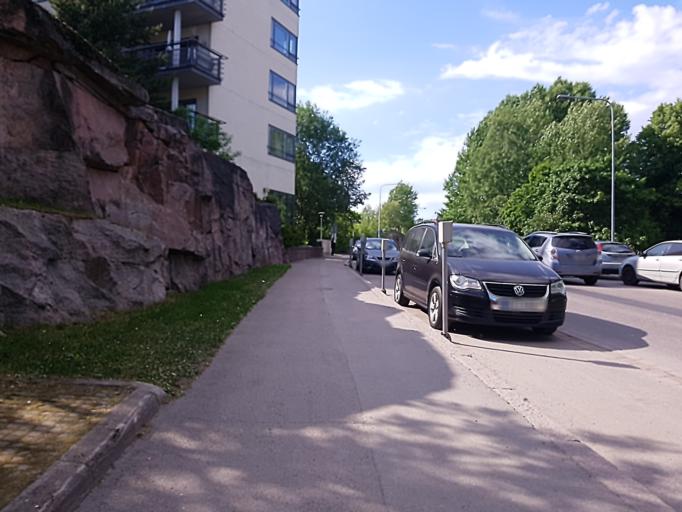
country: FI
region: Uusimaa
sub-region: Helsinki
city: Helsinki
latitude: 60.2133
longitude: 24.9677
